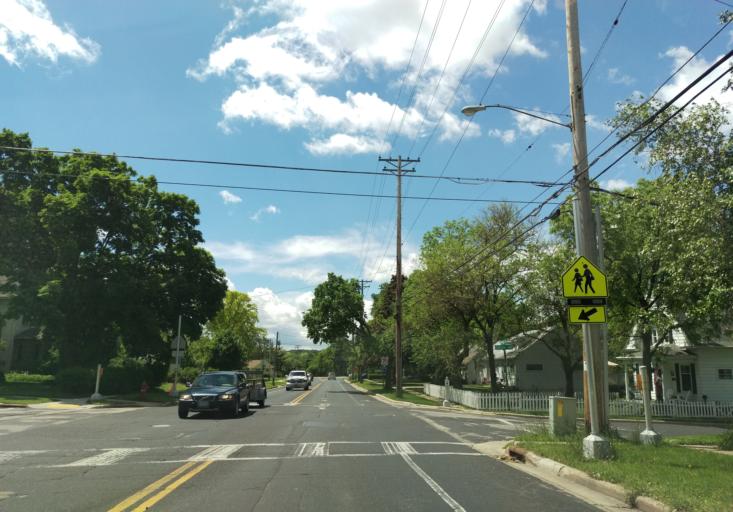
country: US
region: Wisconsin
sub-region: Dane County
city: Middleton
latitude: 43.0937
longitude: -89.5019
